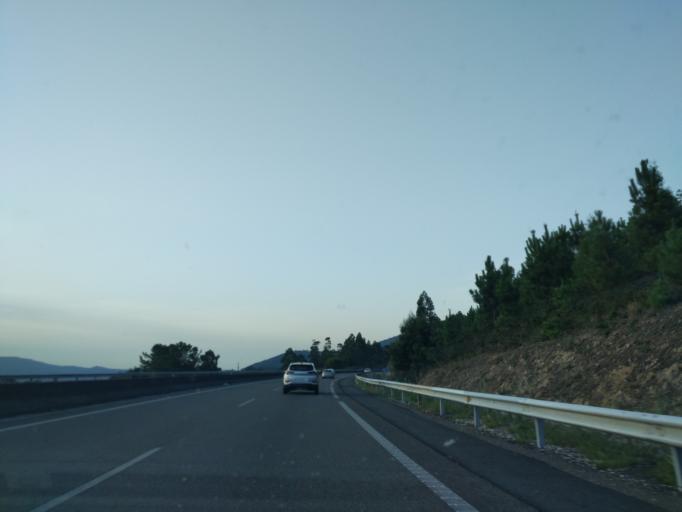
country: ES
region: Galicia
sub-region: Provincia de Pontevedra
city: Valga
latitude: 42.7146
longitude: -8.6436
